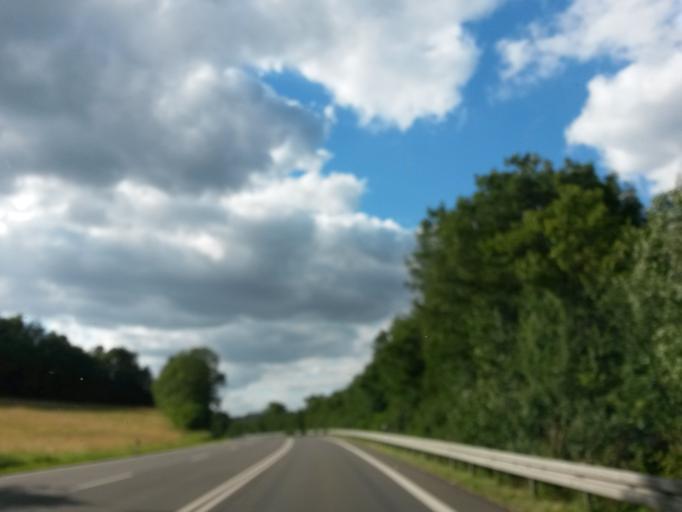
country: DE
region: North Rhine-Westphalia
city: Waldbrol
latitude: 50.9263
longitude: 7.6305
